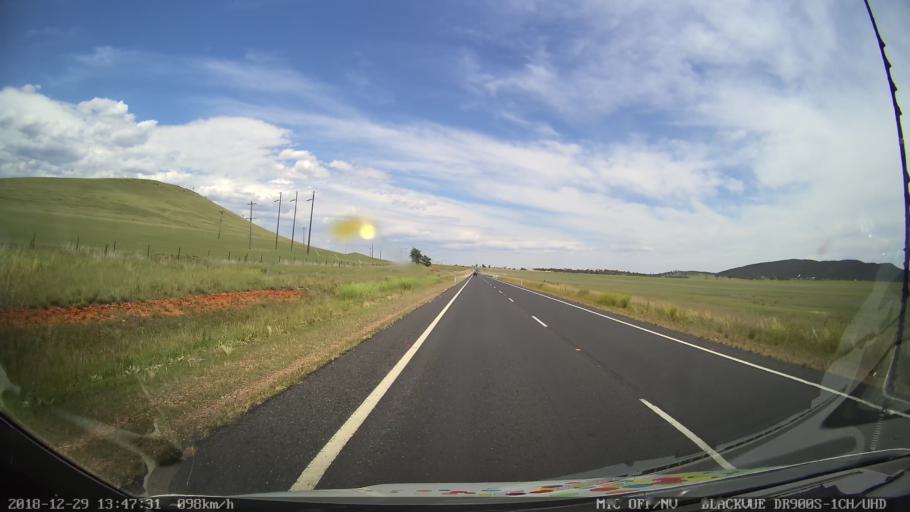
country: AU
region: New South Wales
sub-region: Cooma-Monaro
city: Cooma
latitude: -36.1277
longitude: 149.1432
